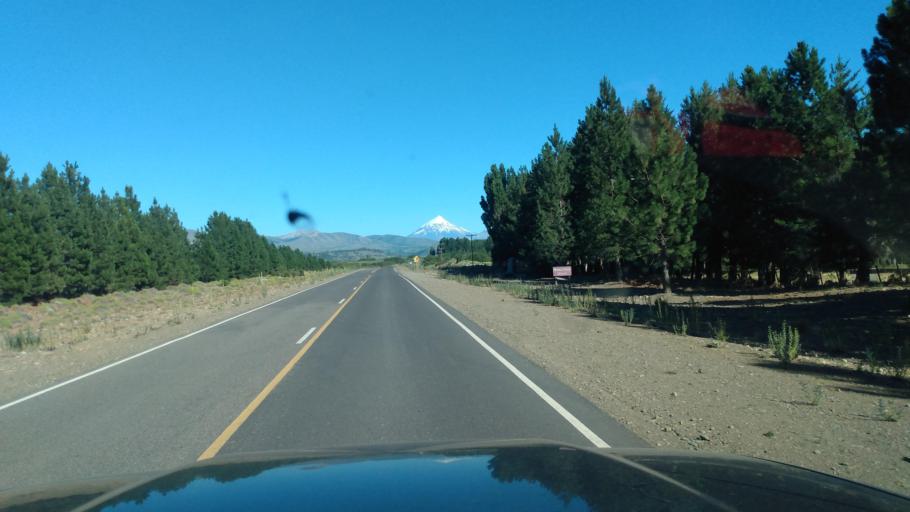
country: AR
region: Neuquen
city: Junin de los Andes
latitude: -39.9024
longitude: -71.1365
